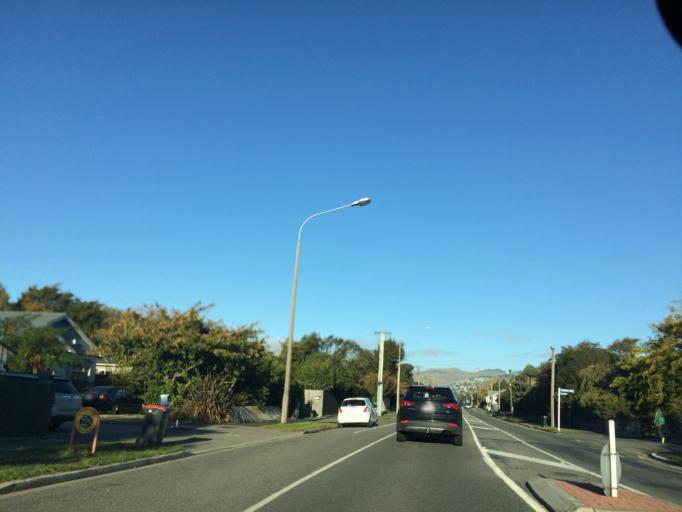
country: NZ
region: Canterbury
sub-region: Christchurch City
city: Christchurch
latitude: -43.5556
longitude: 172.5961
